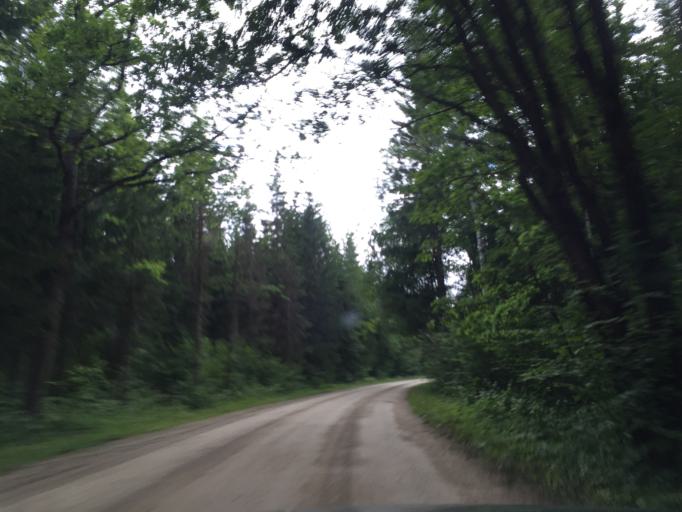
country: LV
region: Malpils
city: Malpils
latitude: 56.9420
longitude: 25.0039
